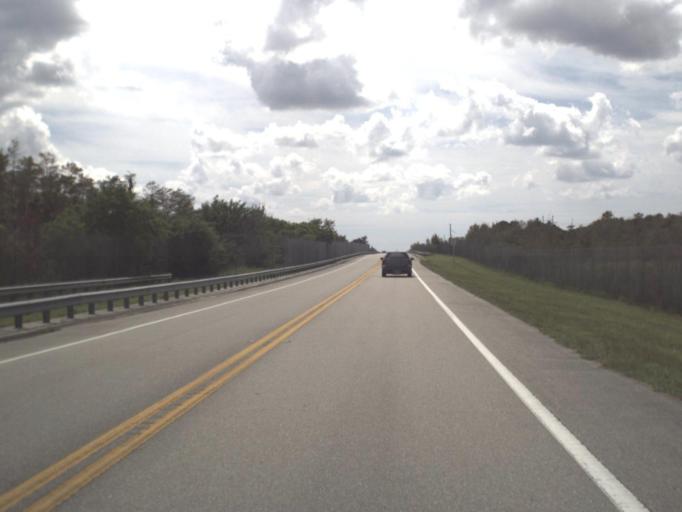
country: US
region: Florida
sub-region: Collier County
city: Lely Resort
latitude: 25.9852
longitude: -81.3481
